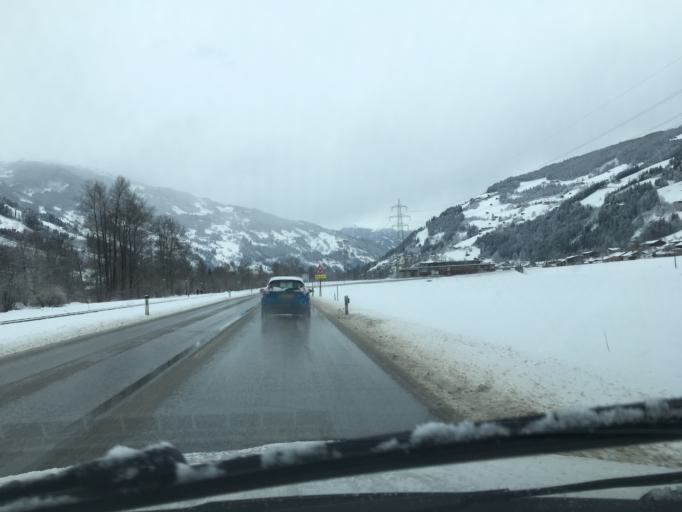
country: AT
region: Tyrol
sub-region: Politischer Bezirk Schwaz
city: Schwendau
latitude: 47.1871
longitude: 11.8666
